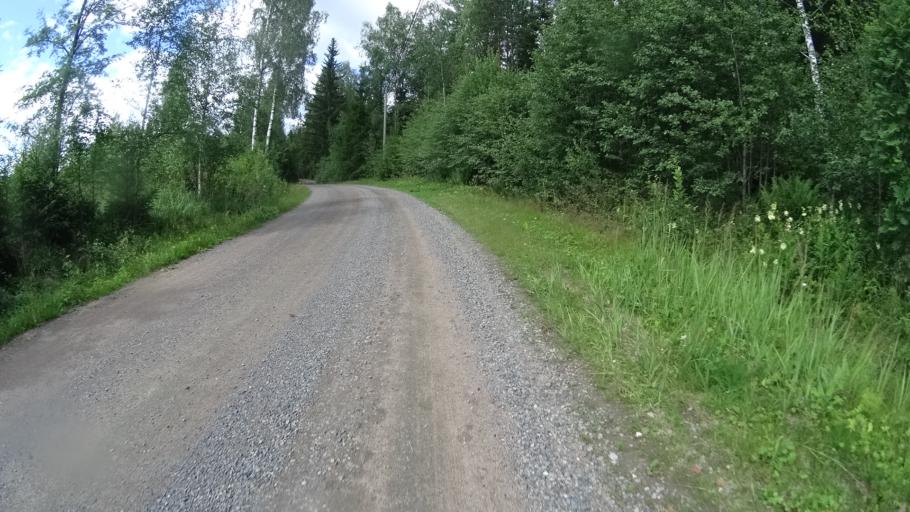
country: FI
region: Uusimaa
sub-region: Helsinki
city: Karkkila
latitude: 60.5973
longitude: 24.2173
